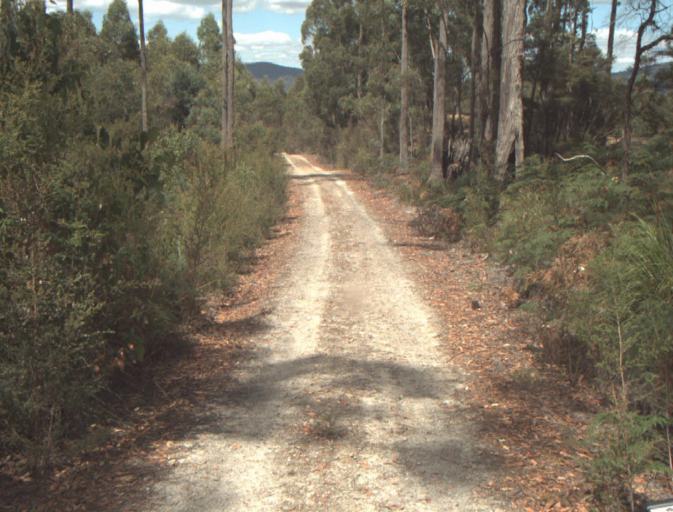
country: AU
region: Tasmania
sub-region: Launceston
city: Mayfield
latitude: -41.2017
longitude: 147.1638
